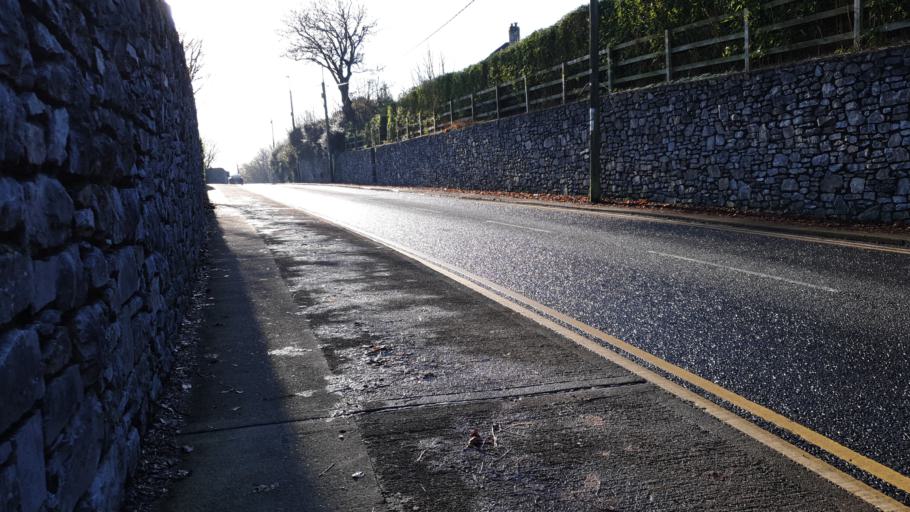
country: IE
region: Munster
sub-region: County Cork
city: Cork
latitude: 51.8930
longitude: -8.4340
